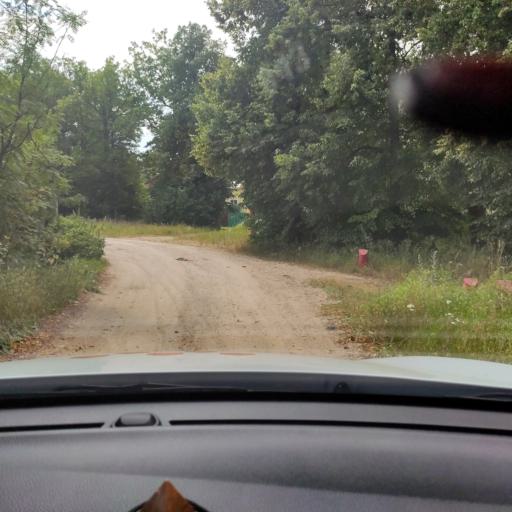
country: RU
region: Tatarstan
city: Osinovo
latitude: 55.9107
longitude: 48.9624
